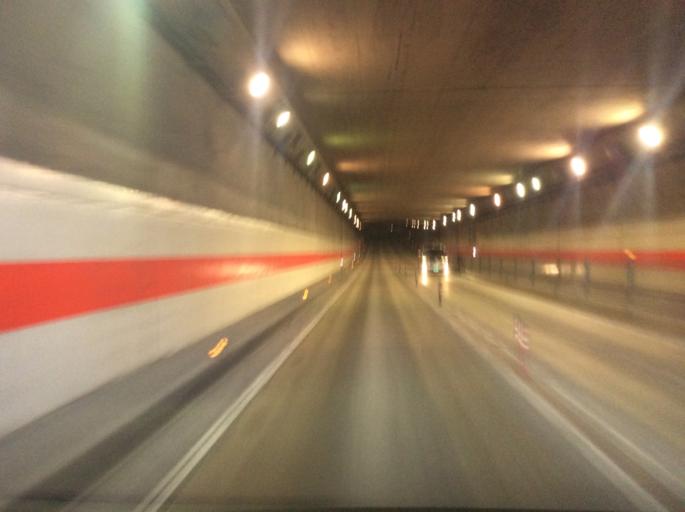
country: JP
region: Miyagi
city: Iwanuma
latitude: 38.1367
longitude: 140.9073
